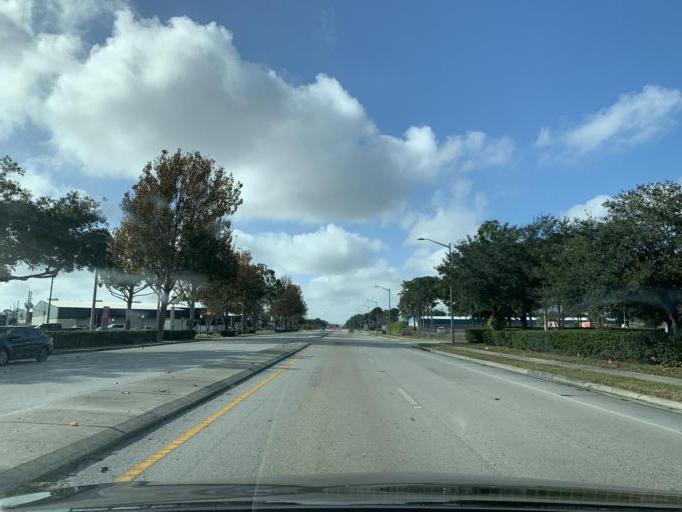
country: US
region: Florida
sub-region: Orange County
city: Oak Ridge
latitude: 28.5042
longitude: -81.4286
